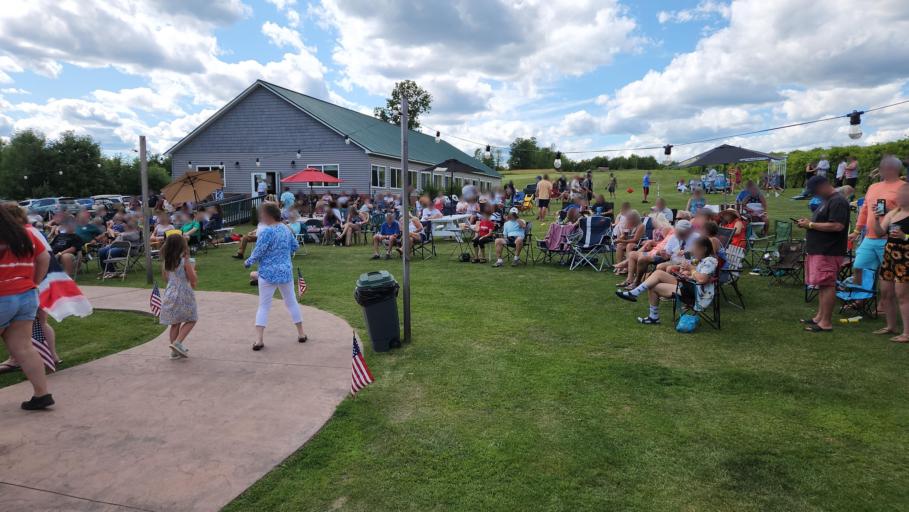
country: CA
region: Ontario
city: Brockville
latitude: 44.5108
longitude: -75.6169
